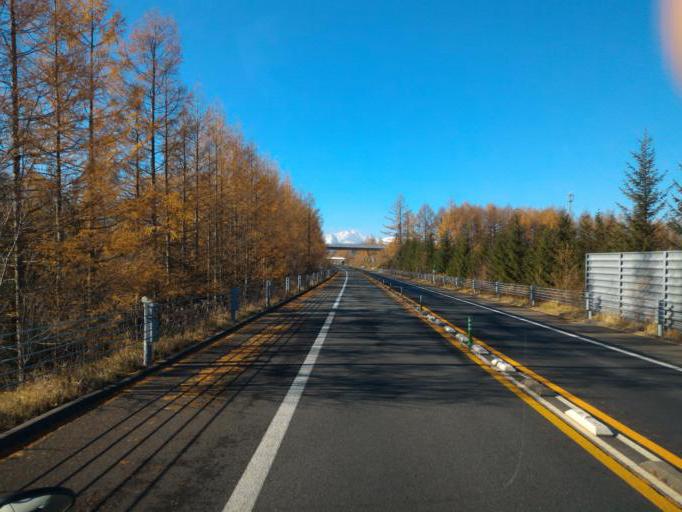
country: JP
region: Hokkaido
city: Otofuke
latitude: 42.9784
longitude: 142.9357
